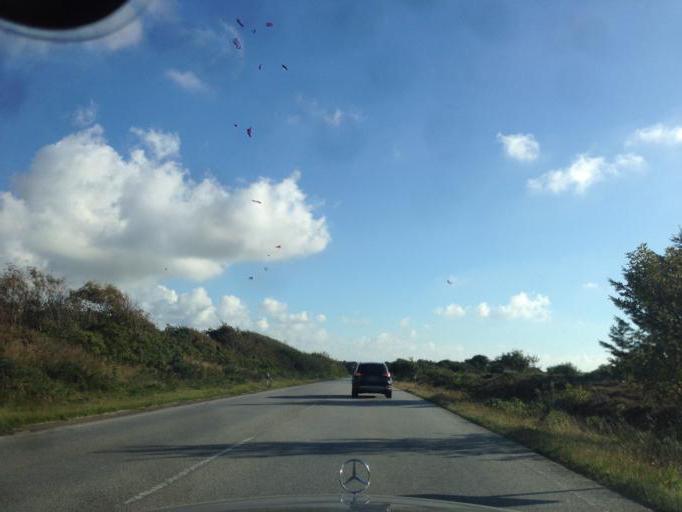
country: DE
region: Schleswig-Holstein
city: Westerland
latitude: 54.9213
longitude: 8.3233
